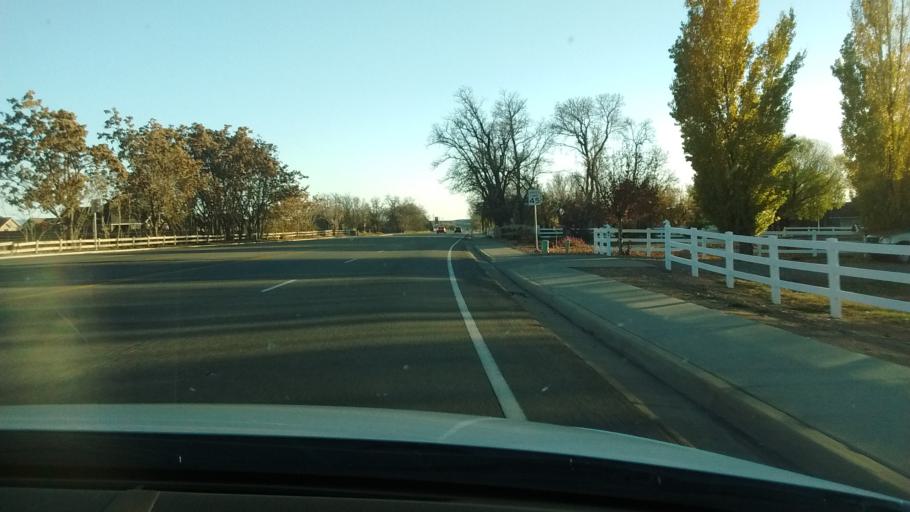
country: US
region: Utah
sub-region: Kane County
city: Kanab
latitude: 37.0363
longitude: -112.5249
